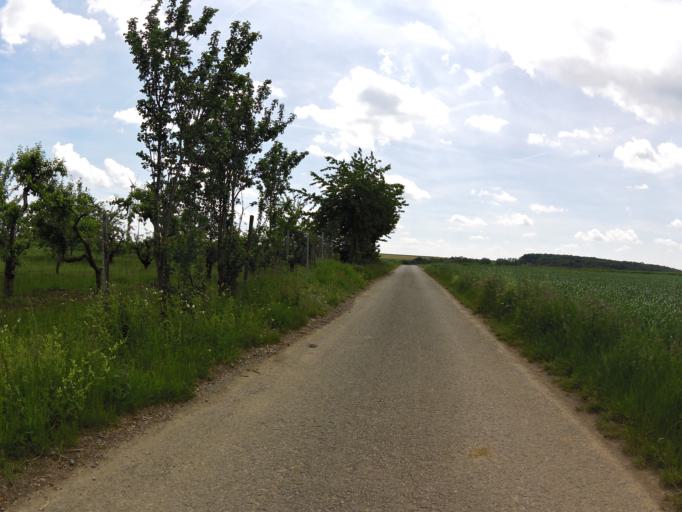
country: DE
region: Bavaria
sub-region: Regierungsbezirk Unterfranken
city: Theilheim
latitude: 49.7267
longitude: 10.0313
